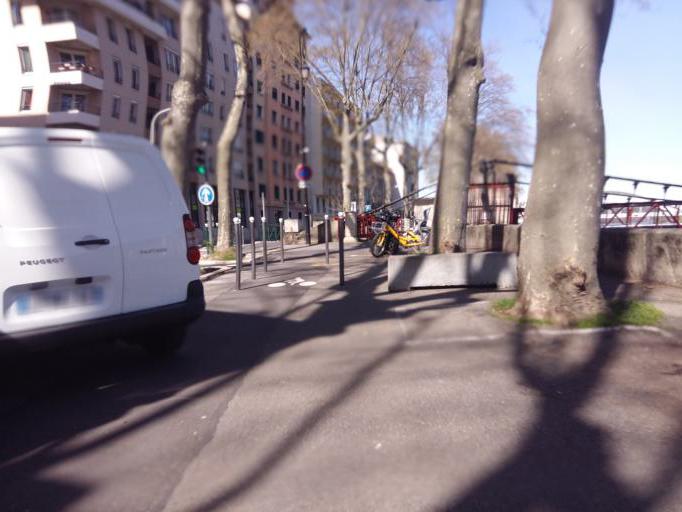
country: FR
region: Rhone-Alpes
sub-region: Departement du Rhone
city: Tassin-la-Demi-Lune
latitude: 45.7782
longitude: 4.8080
